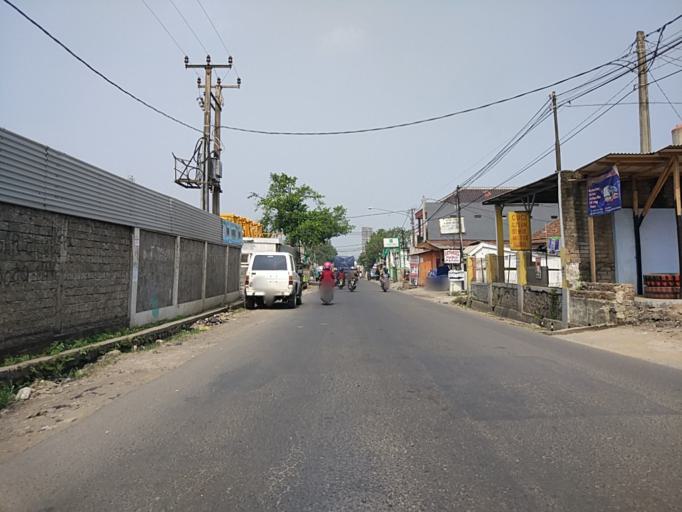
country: ID
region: West Java
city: Padalarang
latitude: -6.8491
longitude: 107.4975
